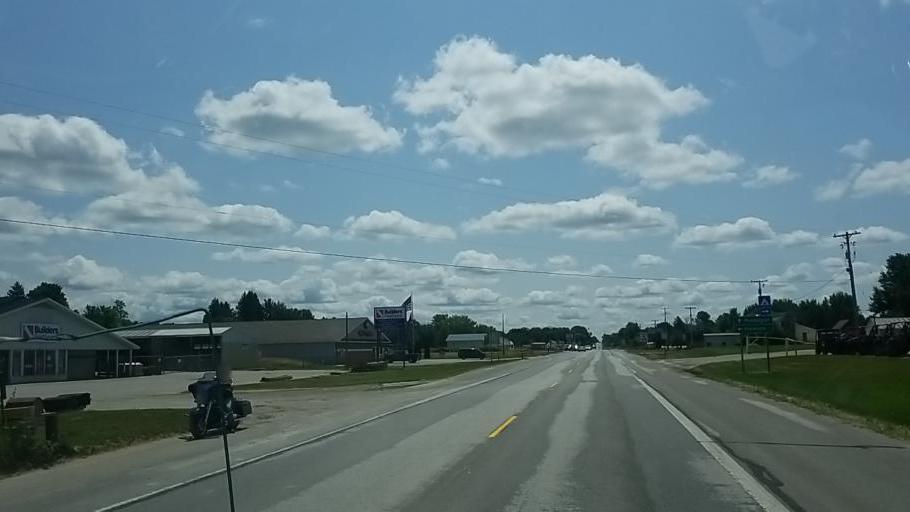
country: US
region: Michigan
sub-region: Newaygo County
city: Fremont
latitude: 43.4693
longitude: -86.0395
